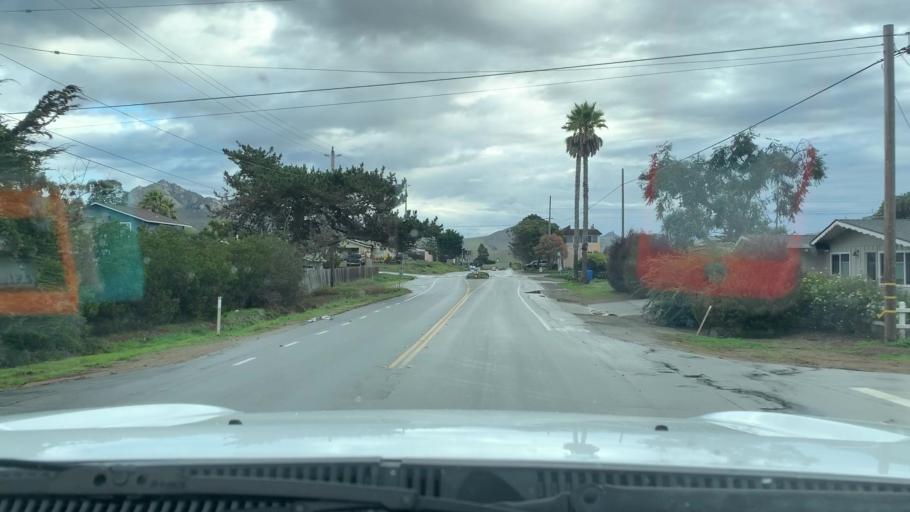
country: US
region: California
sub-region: San Luis Obispo County
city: Los Osos
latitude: 35.3300
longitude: -120.8278
